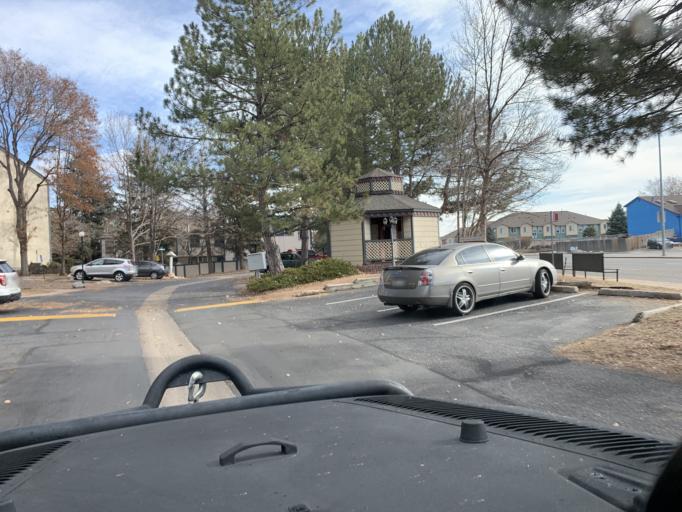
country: US
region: Colorado
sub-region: Adams County
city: Aurora
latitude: 39.7071
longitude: -104.7987
